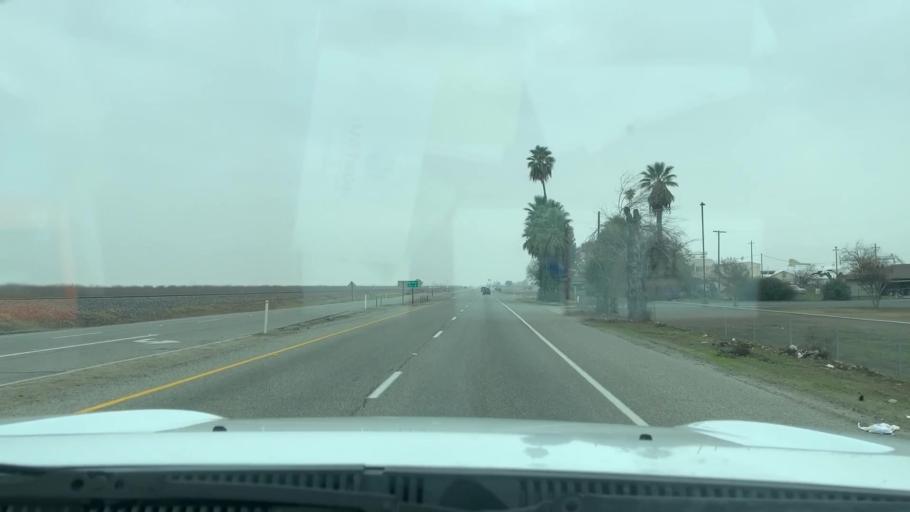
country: US
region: California
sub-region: Kern County
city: Shafter
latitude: 35.5284
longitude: -119.3055
